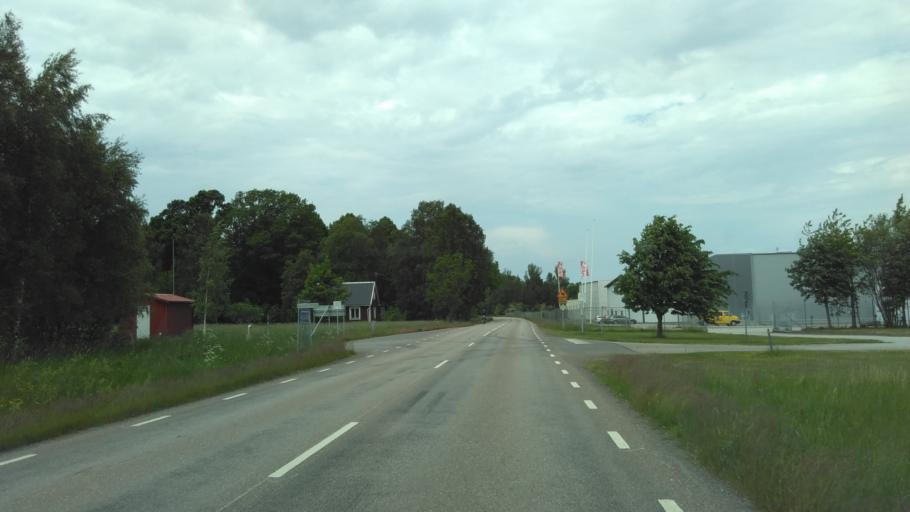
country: SE
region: Vaestra Goetaland
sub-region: Lidkopings Kommun
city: Lidkoping
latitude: 58.4610
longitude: 13.1539
